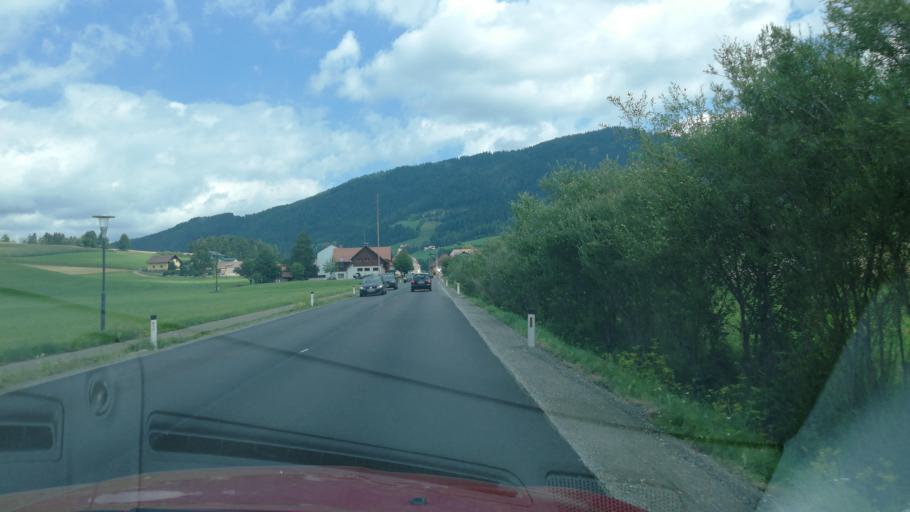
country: AT
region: Styria
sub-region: Politischer Bezirk Murau
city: Perchau am Sattel
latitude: 47.1050
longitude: 14.4564
